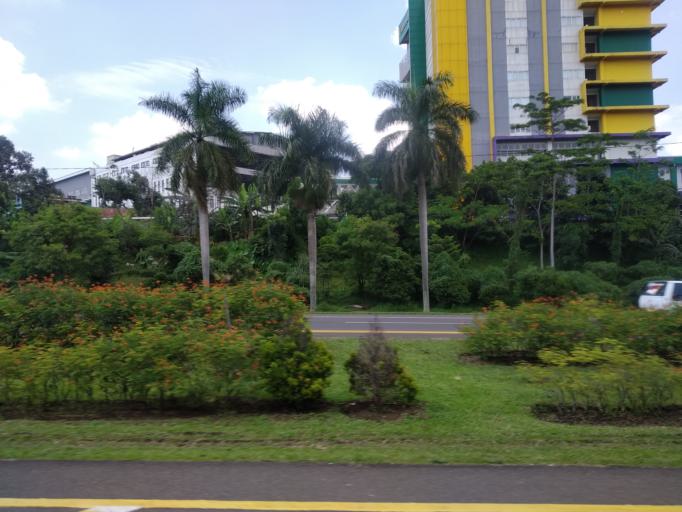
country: ID
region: West Java
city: Bogor
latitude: -6.6010
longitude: 106.8123
